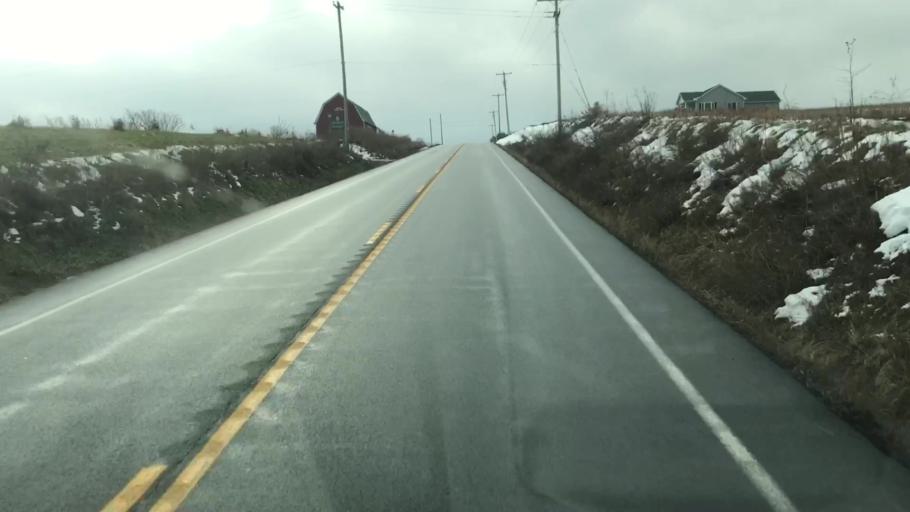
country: US
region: New York
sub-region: Cayuga County
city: Moravia
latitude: 42.8260
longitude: -76.3504
